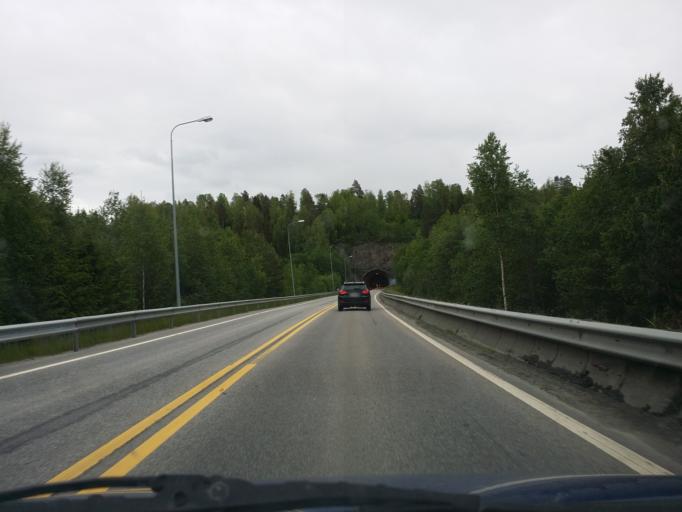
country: NO
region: Hedmark
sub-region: Ringsaker
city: Moelv
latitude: 60.9157
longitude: 10.7144
